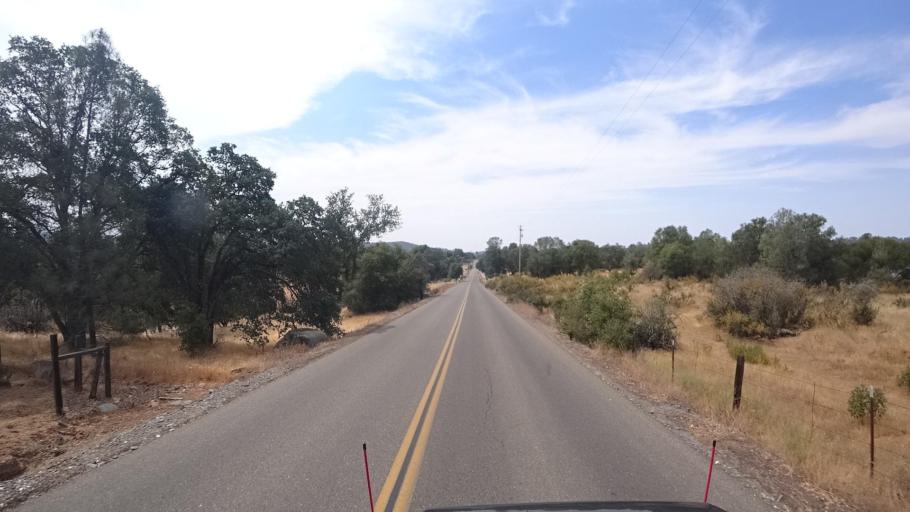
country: US
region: California
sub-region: Mariposa County
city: Midpines
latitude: 37.4766
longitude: -119.8871
